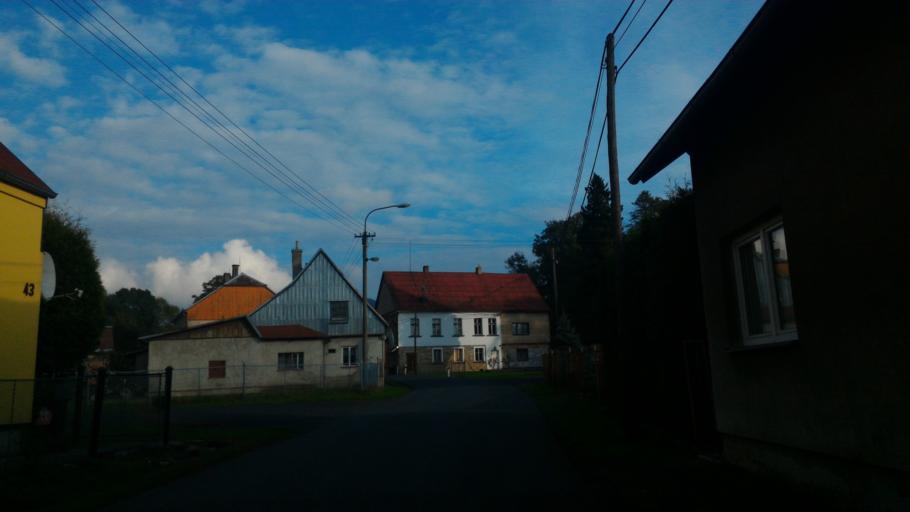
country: CZ
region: Ustecky
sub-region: Okres Decin
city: Chribska
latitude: 50.8575
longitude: 14.5052
